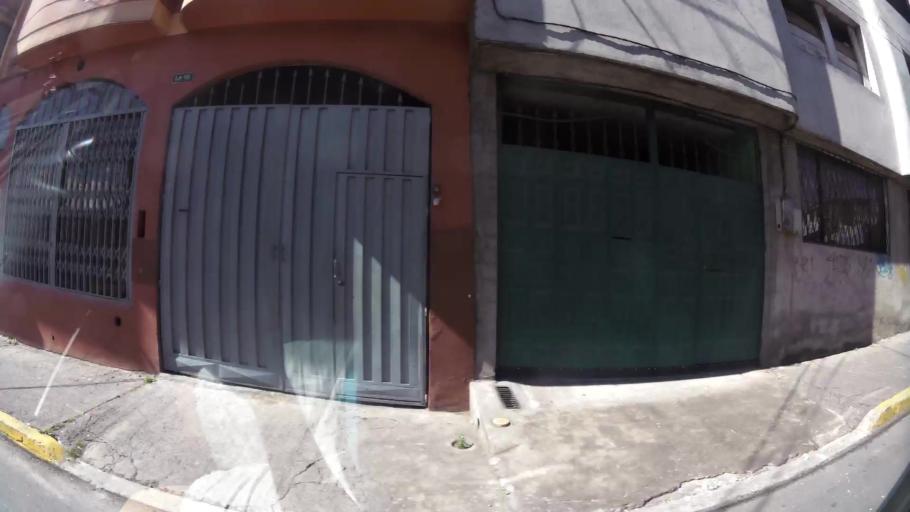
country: EC
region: Pichincha
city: Quito
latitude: -0.2862
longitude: -78.5616
